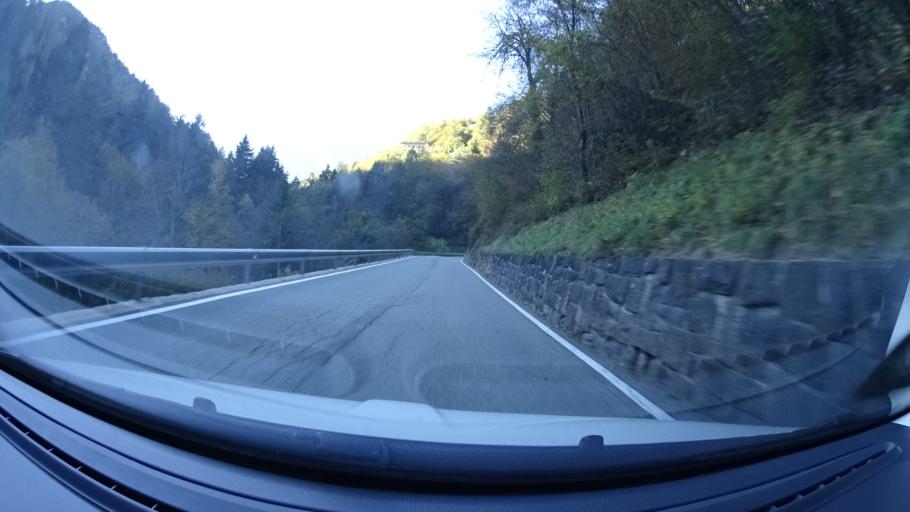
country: IT
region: Trentino-Alto Adige
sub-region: Bolzano
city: Laion
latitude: 46.5973
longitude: 11.5646
